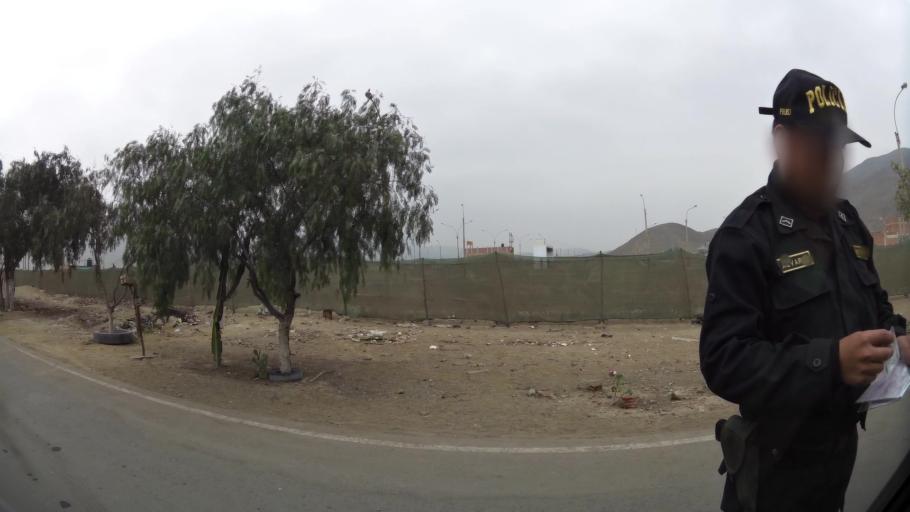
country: PE
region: Lima
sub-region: Lima
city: Santa Rosa
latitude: -11.7901
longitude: -77.1516
